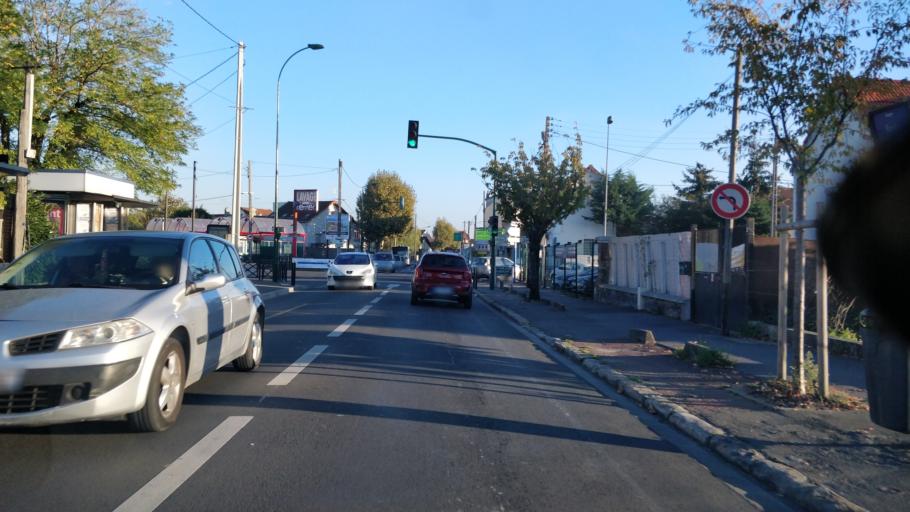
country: FR
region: Ile-de-France
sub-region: Departement de Seine-Saint-Denis
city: Gagny
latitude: 48.8748
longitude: 2.5515
